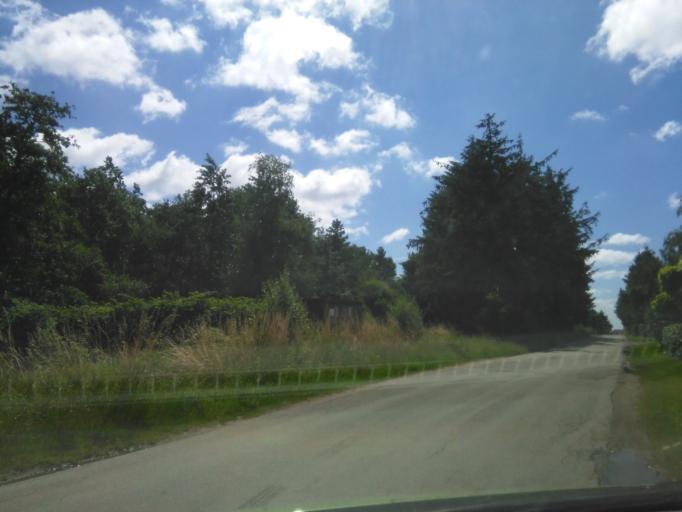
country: DK
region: Central Jutland
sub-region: Arhus Kommune
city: Logten
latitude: 56.1853
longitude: 10.3777
